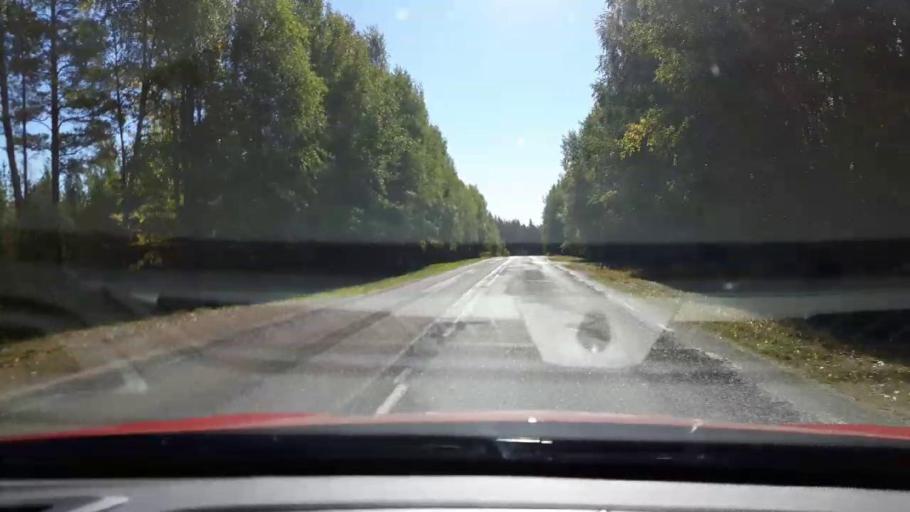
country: SE
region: Jaemtland
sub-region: Harjedalens Kommun
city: Sveg
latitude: 62.1242
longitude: 14.1647
